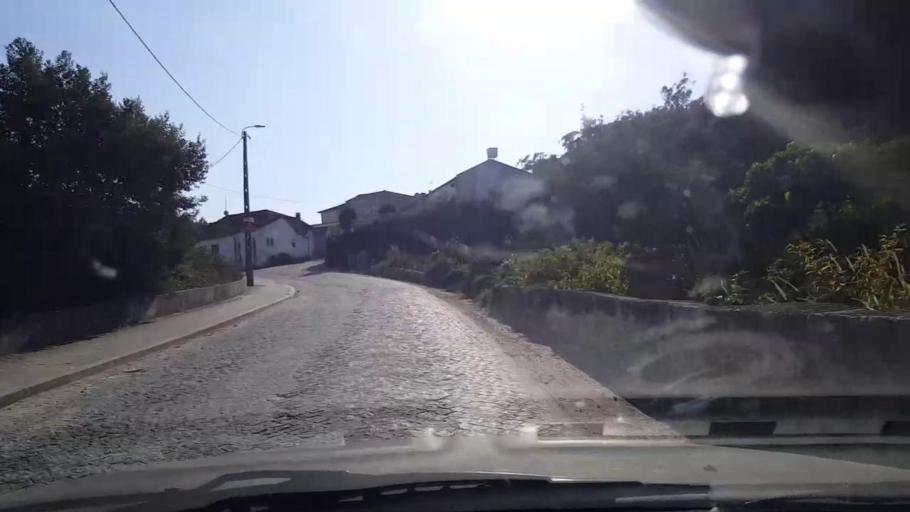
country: PT
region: Porto
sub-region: Vila do Conde
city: Arvore
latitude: 41.3583
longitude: -8.7216
